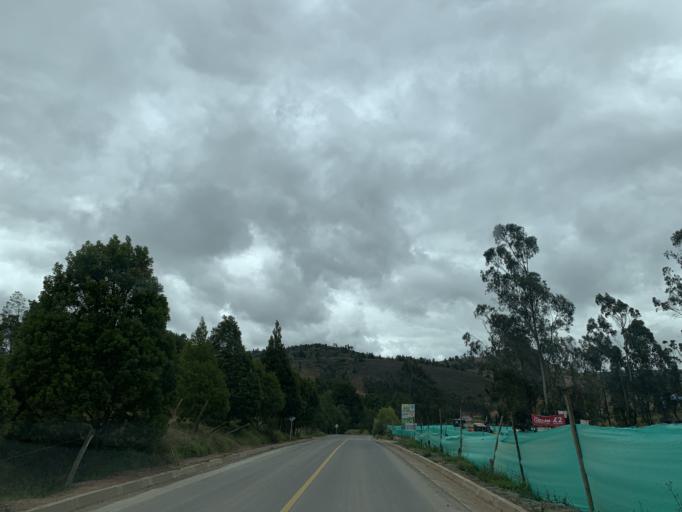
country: CO
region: Boyaca
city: Tunja
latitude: 5.5292
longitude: -73.3302
